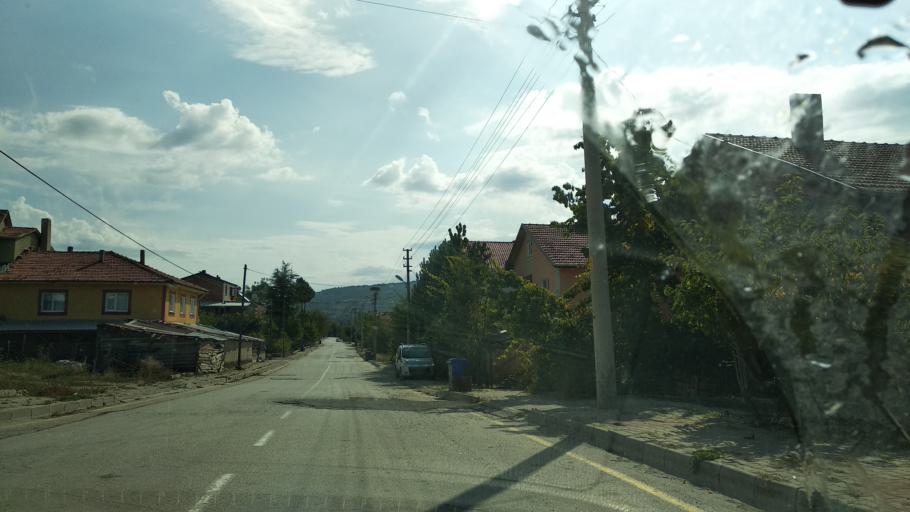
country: TR
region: Bolu
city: Seben
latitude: 40.4132
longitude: 31.5672
